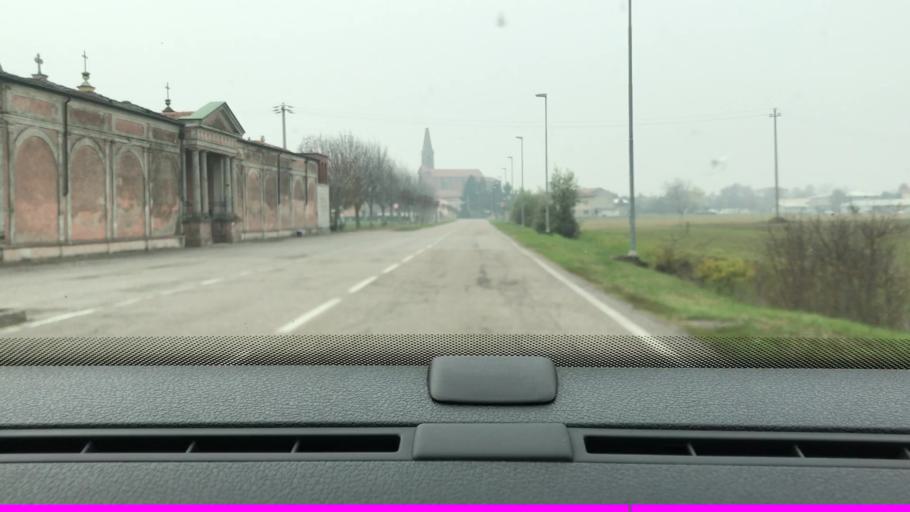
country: IT
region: Lombardy
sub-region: Provincia di Mantova
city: San Giacomo delle Segnate
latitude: 44.9693
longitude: 11.0390
